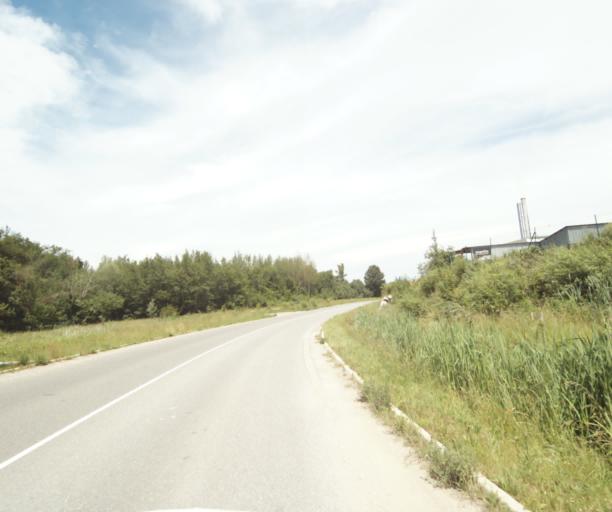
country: FR
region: Rhone-Alpes
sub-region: Departement de la Haute-Savoie
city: Margencel
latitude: 46.3245
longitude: 6.4353
